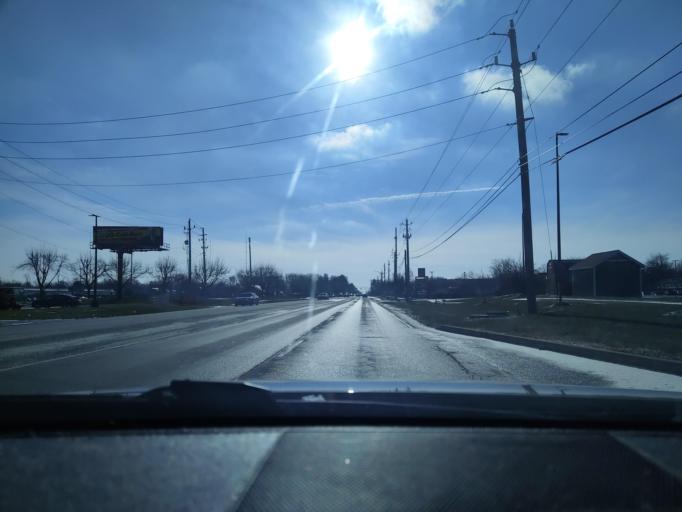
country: US
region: Indiana
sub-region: Boone County
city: Zionsville
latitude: 39.9085
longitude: -86.2213
